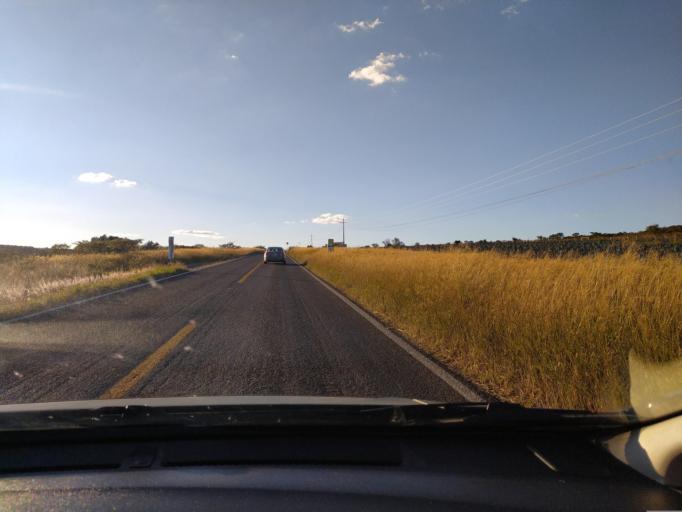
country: MX
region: Jalisco
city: San Julian
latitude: 21.0024
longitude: -102.1052
